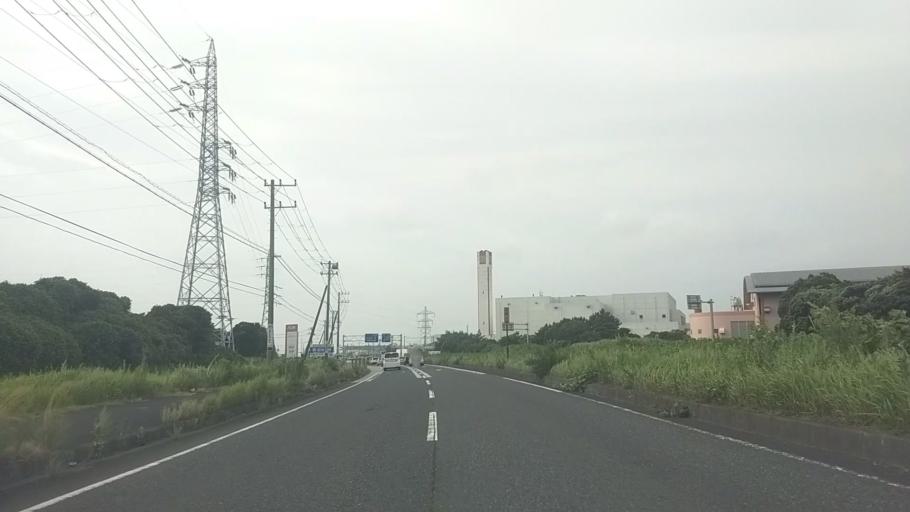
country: JP
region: Chiba
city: Kisarazu
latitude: 35.3673
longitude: 139.9114
